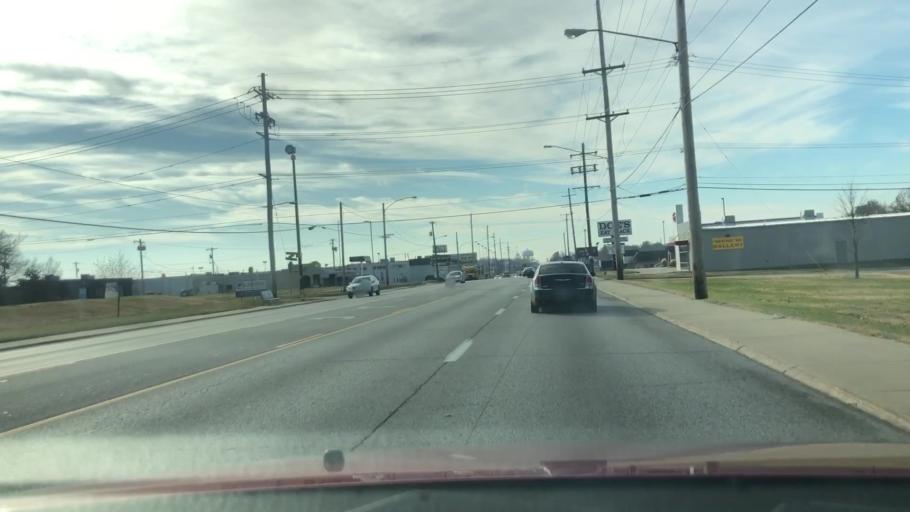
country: US
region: Missouri
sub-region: Greene County
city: Springfield
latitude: 37.2188
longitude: -93.2617
